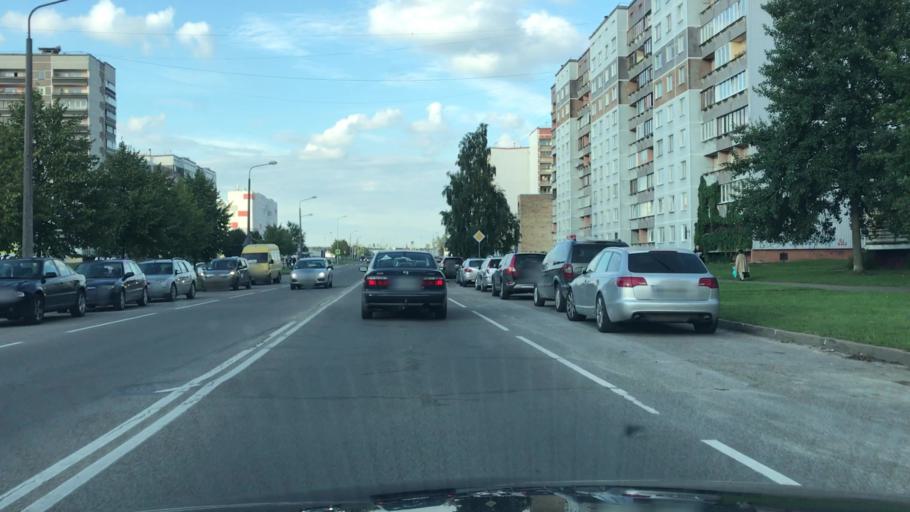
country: LV
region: Stopini
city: Ulbroka
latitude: 56.9420
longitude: 24.2163
